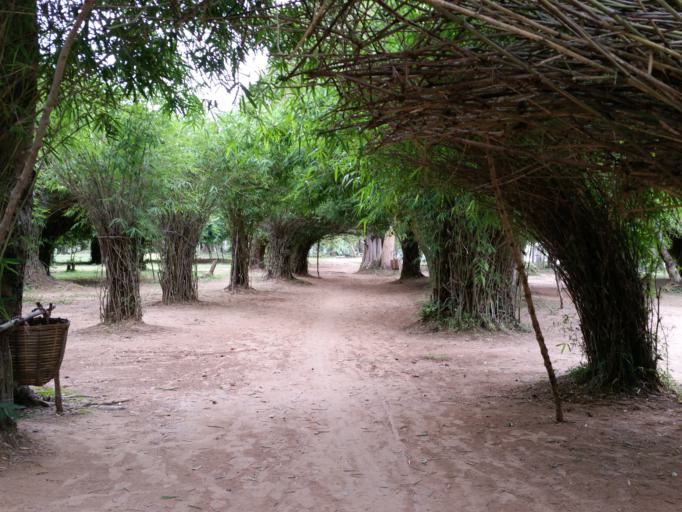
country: LA
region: Champasak
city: Khong
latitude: 13.9536
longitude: 105.9157
